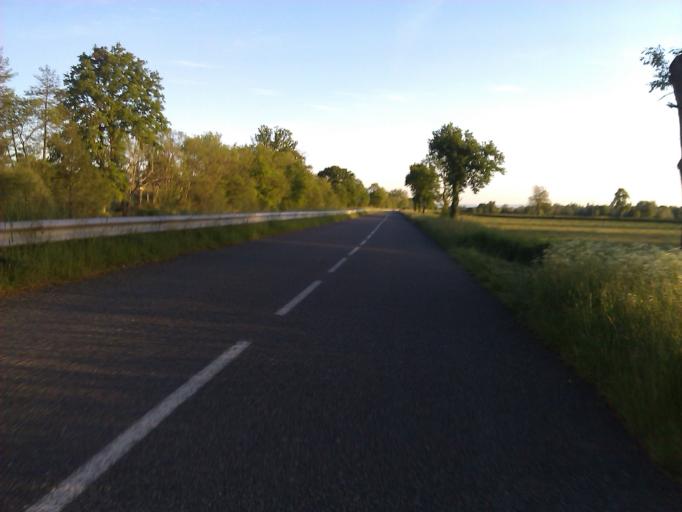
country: FR
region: Bourgogne
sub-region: Departement de Saone-et-Loire
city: Paray-le-Monial
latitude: 46.4901
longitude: 4.1808
